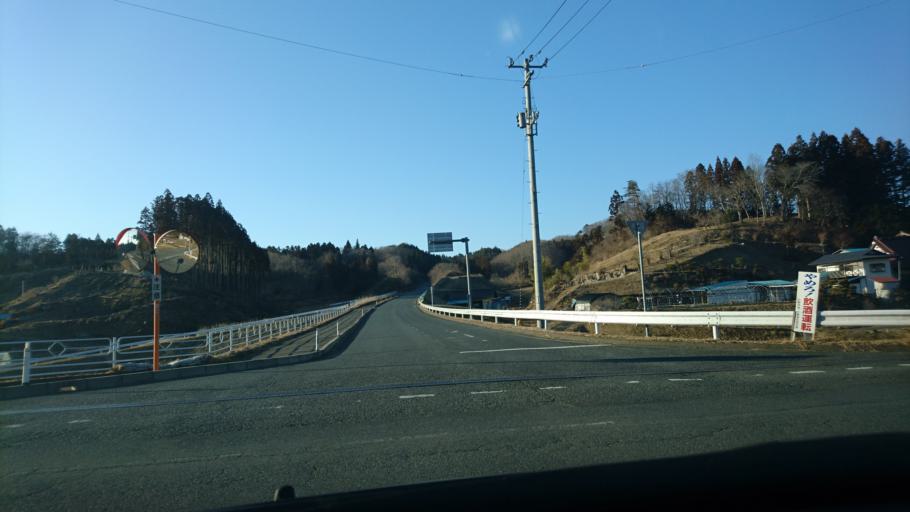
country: JP
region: Iwate
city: Ichinoseki
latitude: 38.9114
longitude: 141.3788
